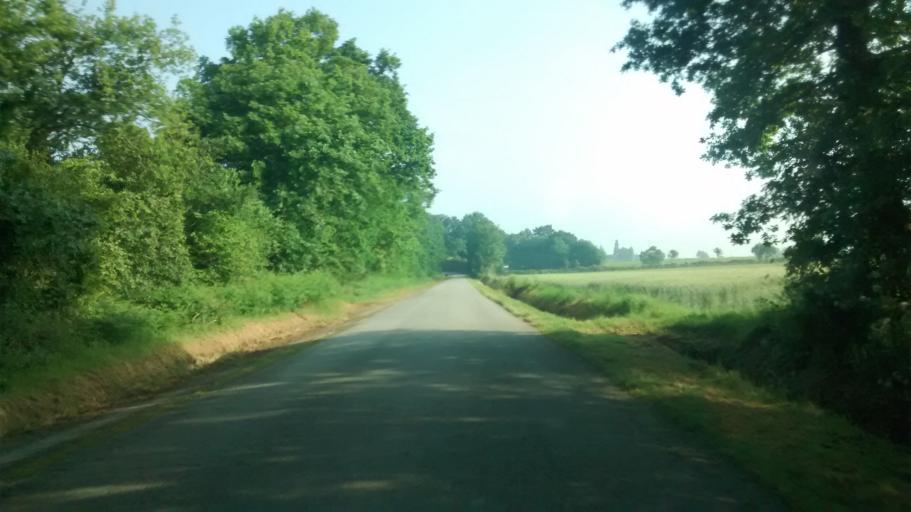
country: FR
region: Brittany
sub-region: Departement du Morbihan
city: Ruffiac
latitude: 47.8394
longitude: -2.2740
